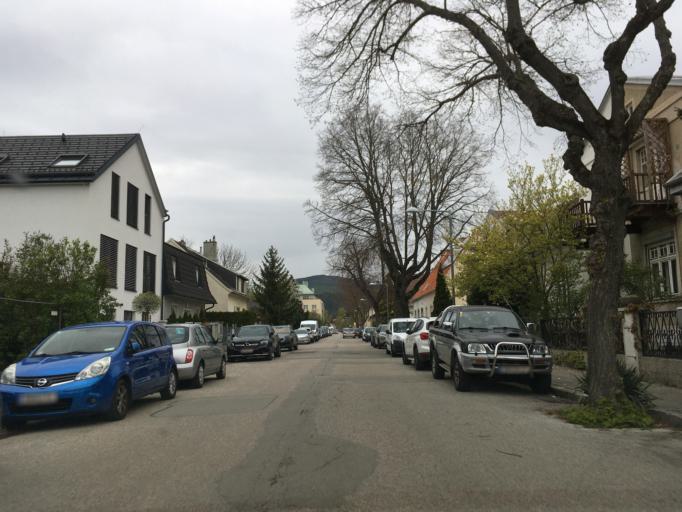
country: AT
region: Lower Austria
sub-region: Politischer Bezirk Baden
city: Baden
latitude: 47.9993
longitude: 16.2320
